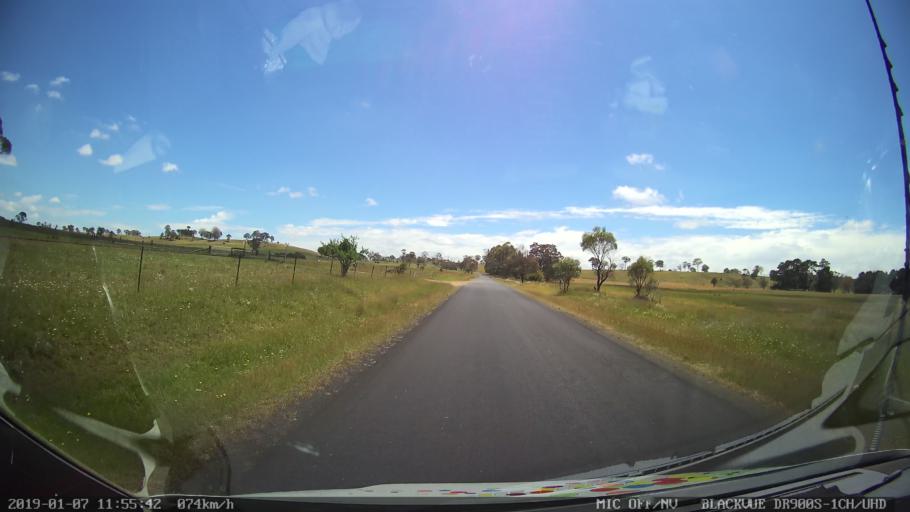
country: AU
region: New South Wales
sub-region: Guyra
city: Guyra
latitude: -30.2826
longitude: 151.6713
